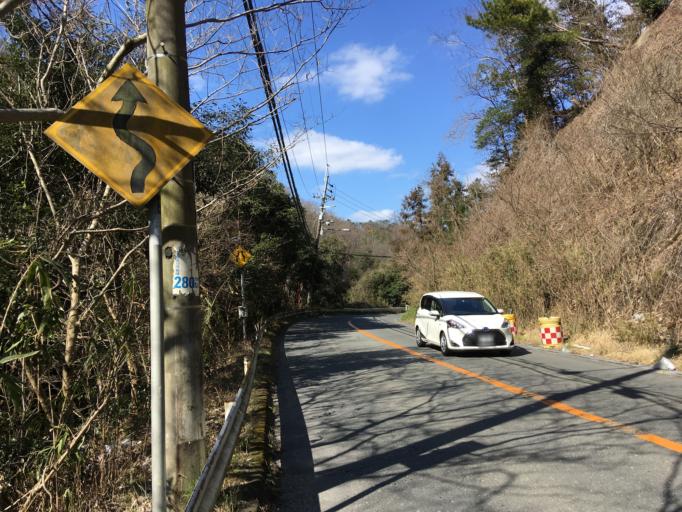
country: JP
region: Osaka
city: Neyagawa
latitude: 34.7531
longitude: 135.6895
